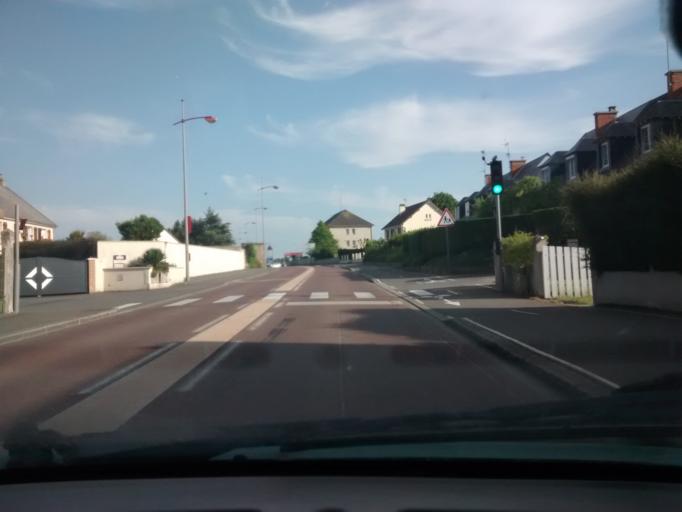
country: FR
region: Lower Normandy
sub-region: Departement de la Manche
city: Lessay
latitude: 49.2154
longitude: -1.5310
